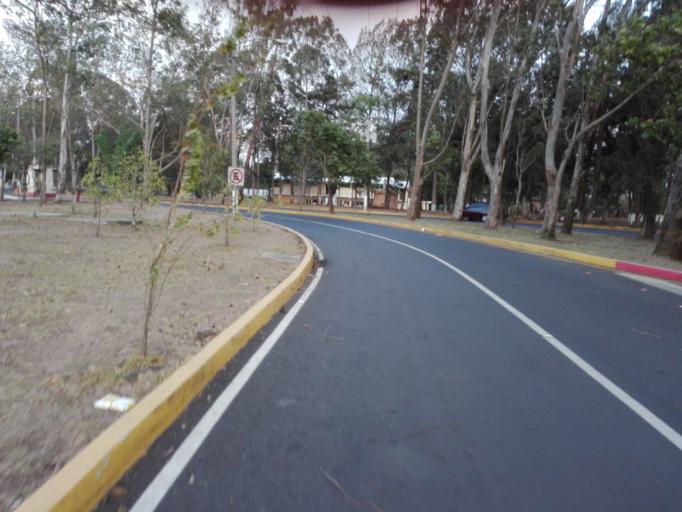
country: GT
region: Guatemala
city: Santa Catarina Pinula
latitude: 14.5817
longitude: -90.5551
